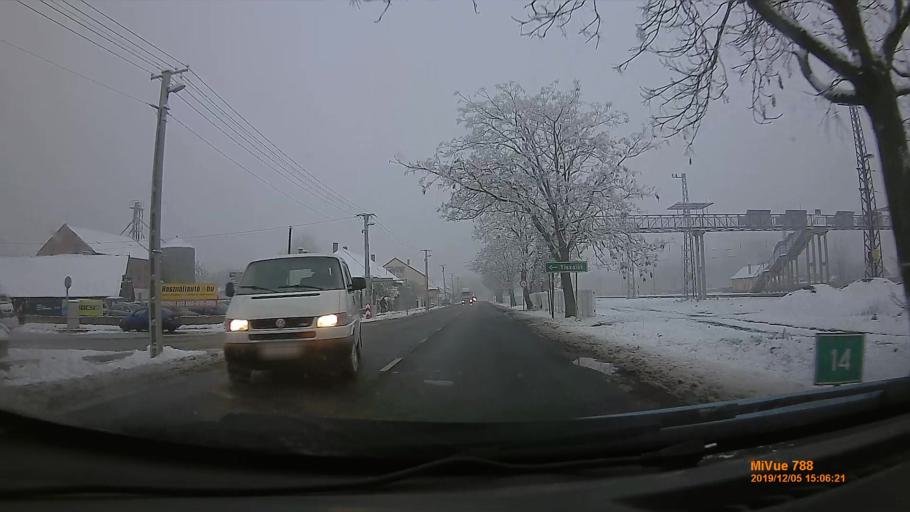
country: HU
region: Szabolcs-Szatmar-Bereg
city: Rakamaz
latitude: 48.1175
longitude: 21.4782
